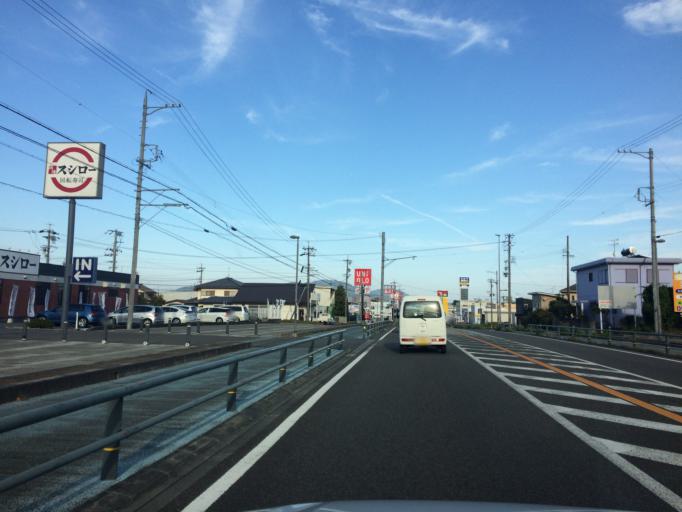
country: JP
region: Shizuoka
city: Fujieda
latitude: 34.8500
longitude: 138.2378
